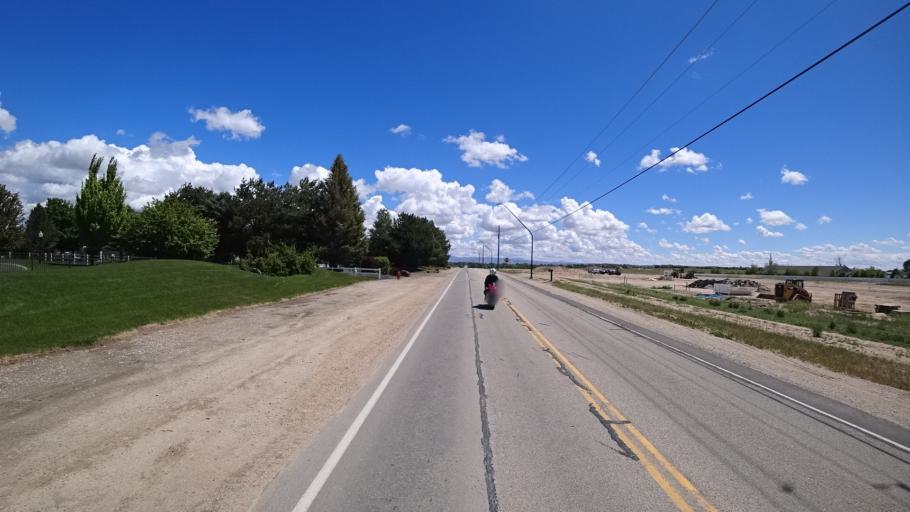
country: US
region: Idaho
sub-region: Ada County
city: Meridian
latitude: 43.5465
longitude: -116.3583
